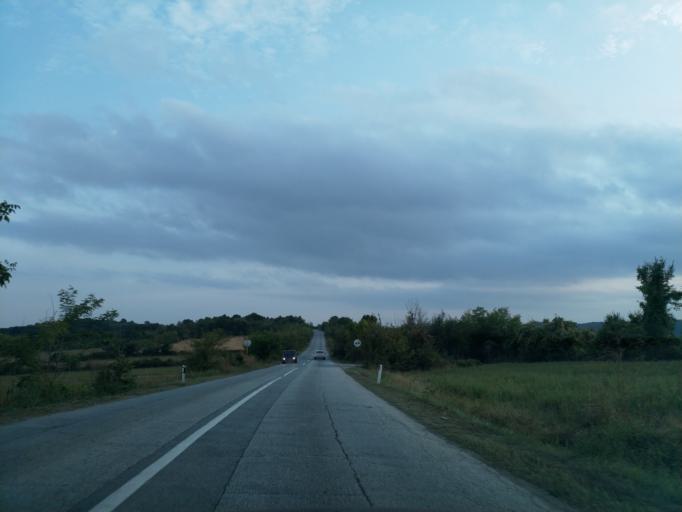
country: RS
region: Central Serbia
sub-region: Sumadijski Okrug
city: Topola
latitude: 44.1524
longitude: 20.7416
